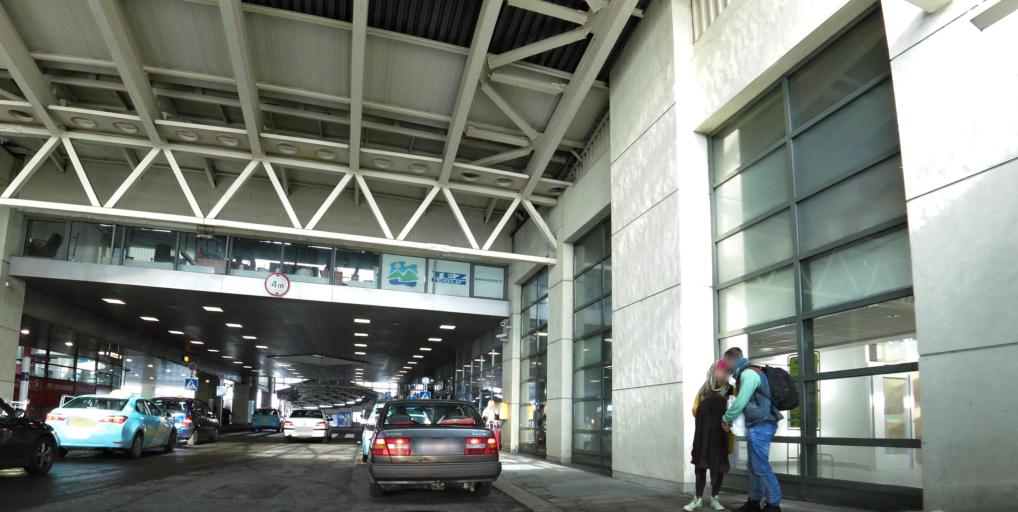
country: LT
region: Vilnius County
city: Naujamiestis
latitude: 54.6424
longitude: 25.2803
